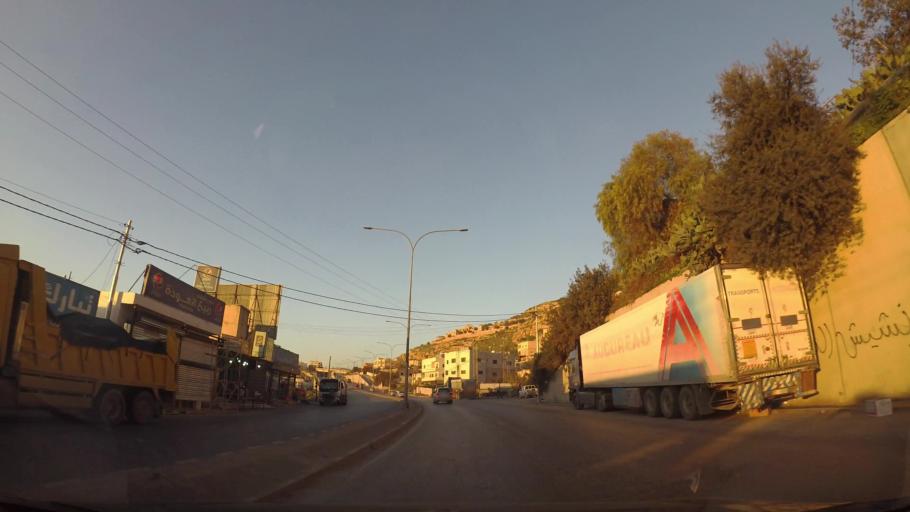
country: JO
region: Amman
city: Umm as Summaq
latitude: 31.8626
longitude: 35.7618
